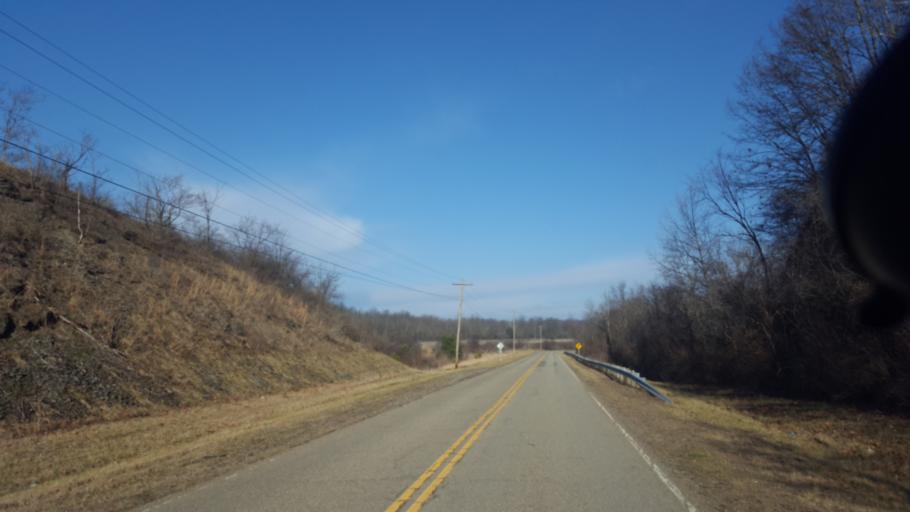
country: US
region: Ohio
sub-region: Guernsey County
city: Cambridge
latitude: 40.1001
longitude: -81.5610
